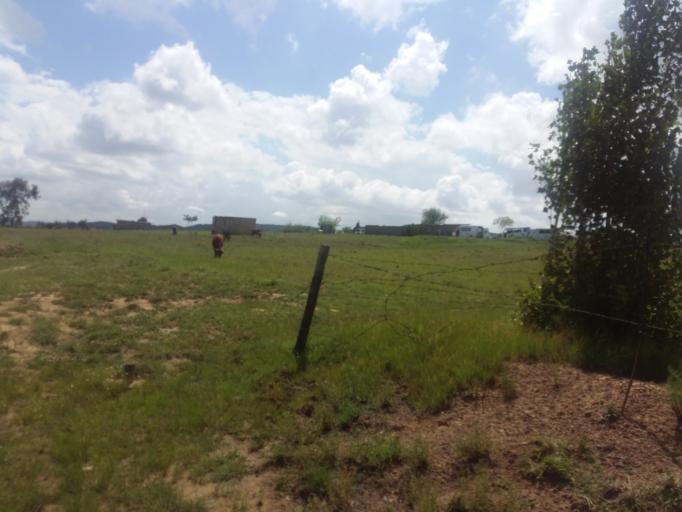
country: LS
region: Mafeteng
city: Mafeteng
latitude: -29.7485
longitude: 27.1123
